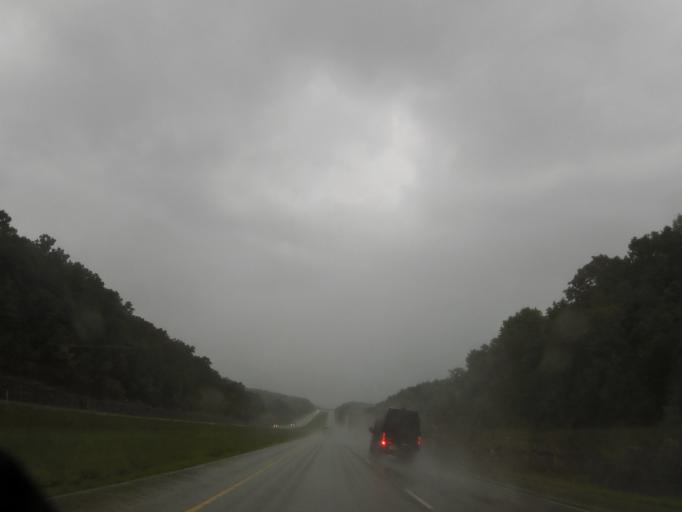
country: US
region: Illinois
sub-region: Johnson County
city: Goreville
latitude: 37.5051
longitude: -88.9018
